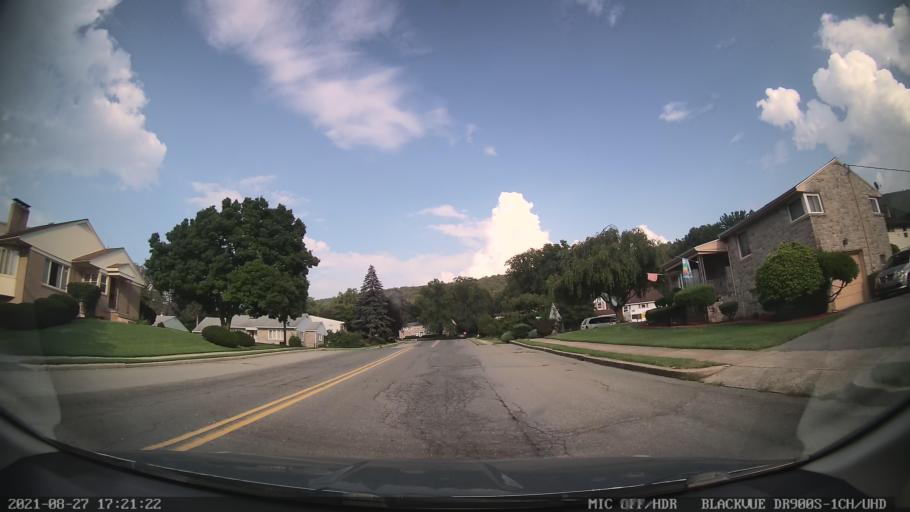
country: US
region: Pennsylvania
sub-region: Berks County
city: Hyde Park
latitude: 40.3636
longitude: -75.9053
